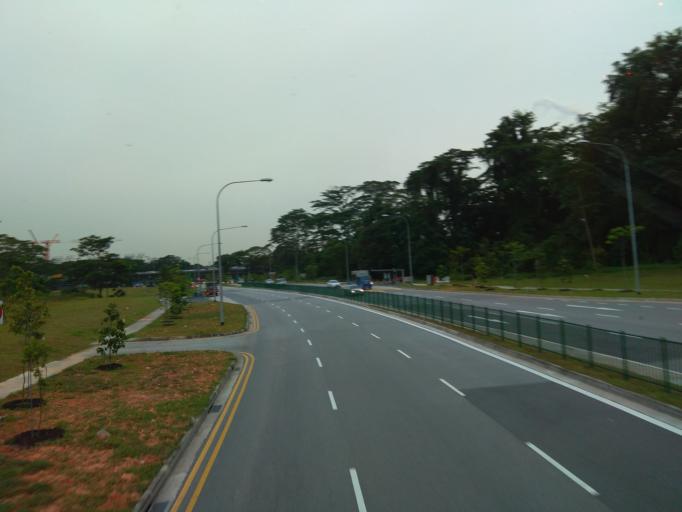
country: MY
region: Johor
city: Johor Bahru
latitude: 1.3571
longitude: 103.6954
